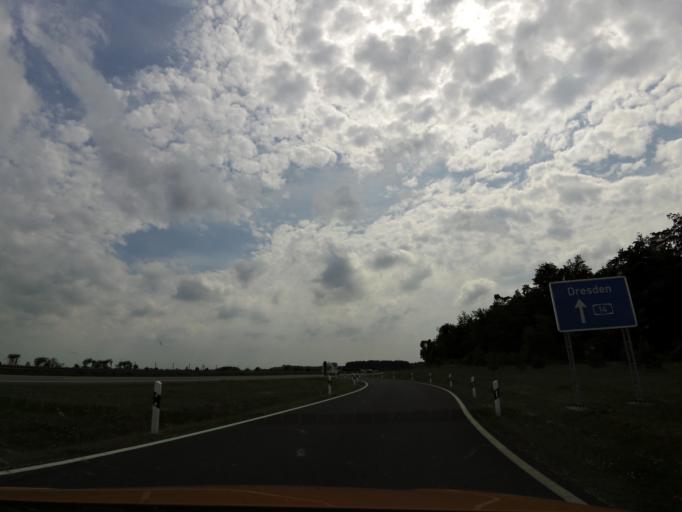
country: DE
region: Mecklenburg-Vorpommern
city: Plate
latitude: 53.5373
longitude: 11.4691
